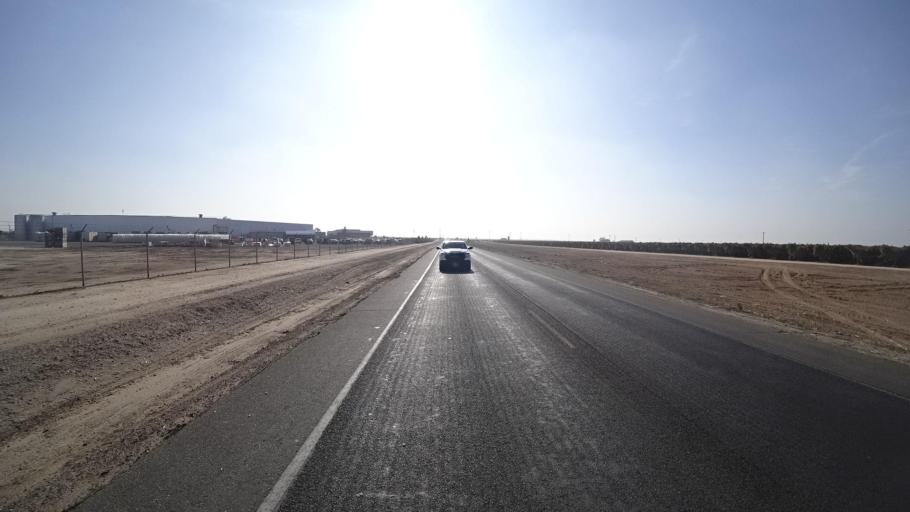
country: US
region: California
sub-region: Kern County
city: McFarland
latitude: 35.7209
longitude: -119.1578
